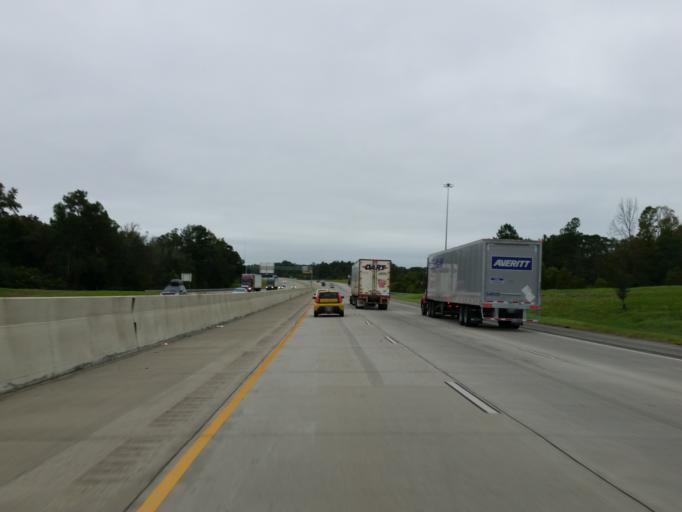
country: US
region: Georgia
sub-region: Crisp County
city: Cordele
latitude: 31.9333
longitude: -83.7474
